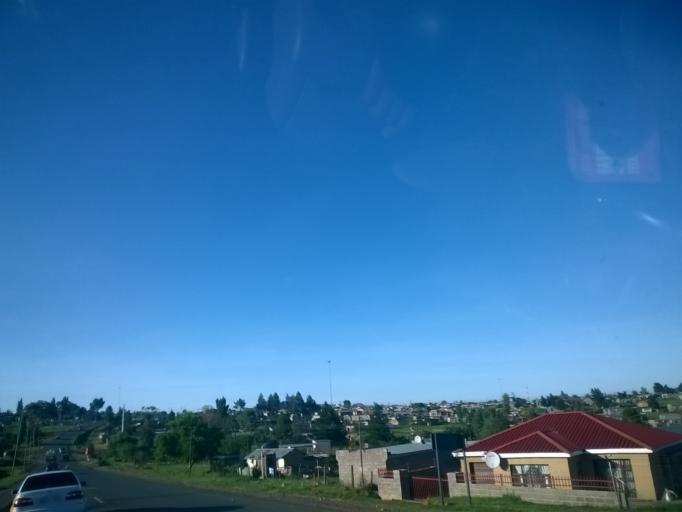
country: LS
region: Maseru
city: Maseru
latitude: -29.2795
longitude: 27.5287
